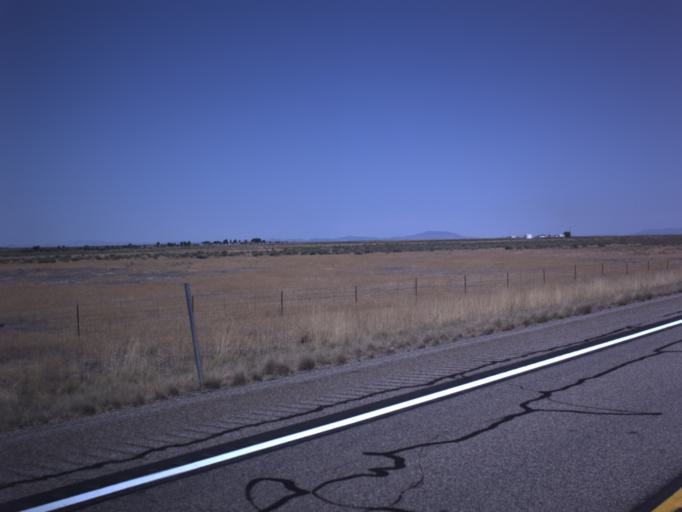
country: US
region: Utah
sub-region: Millard County
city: Delta
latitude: 39.3585
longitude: -112.4965
